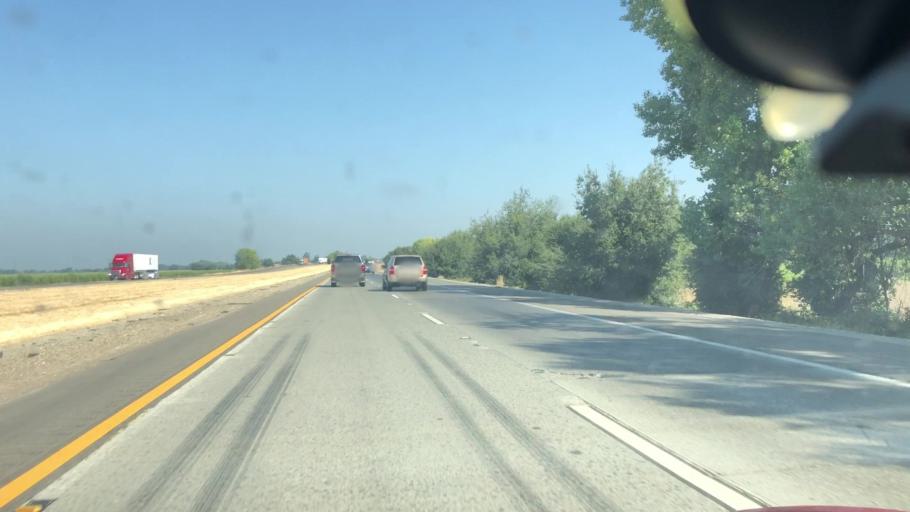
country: US
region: California
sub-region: San Joaquin County
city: Thornton
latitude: 38.2403
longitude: -121.4408
